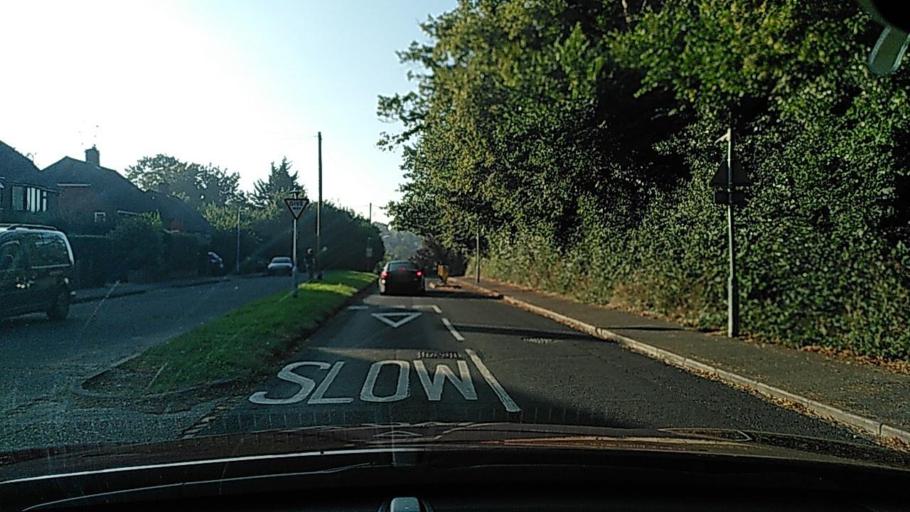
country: GB
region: England
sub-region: Reading
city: Reading
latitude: 51.4807
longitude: -0.9727
